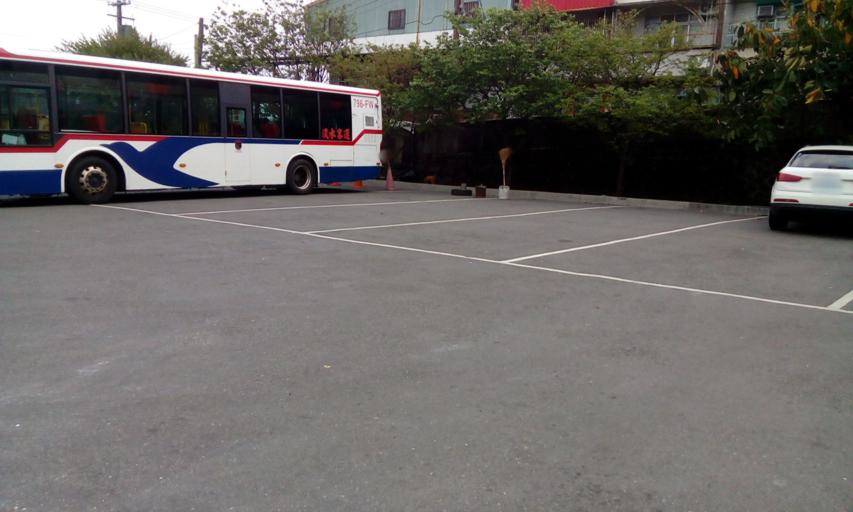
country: TW
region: Taipei
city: Taipei
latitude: 25.1868
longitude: 121.4844
